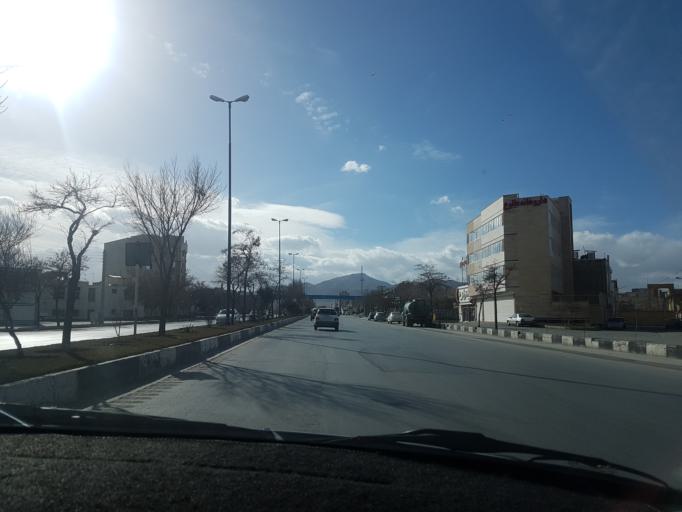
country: IR
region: Markazi
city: Arak
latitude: 34.1181
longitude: 49.7007
